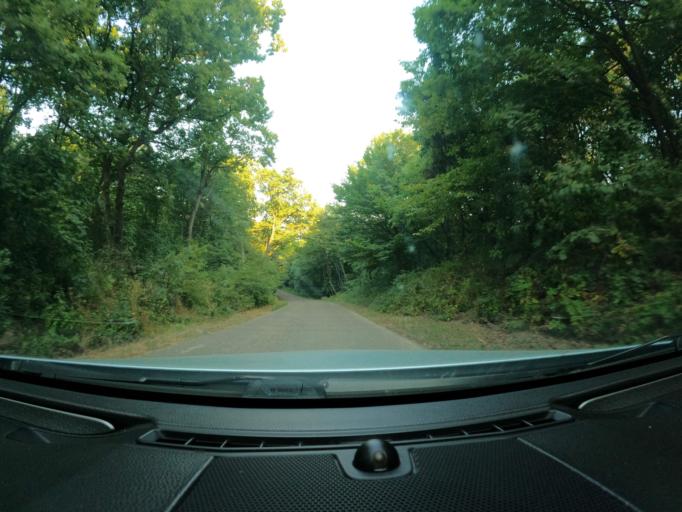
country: RS
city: Vrdnik
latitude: 45.1594
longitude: 19.7710
